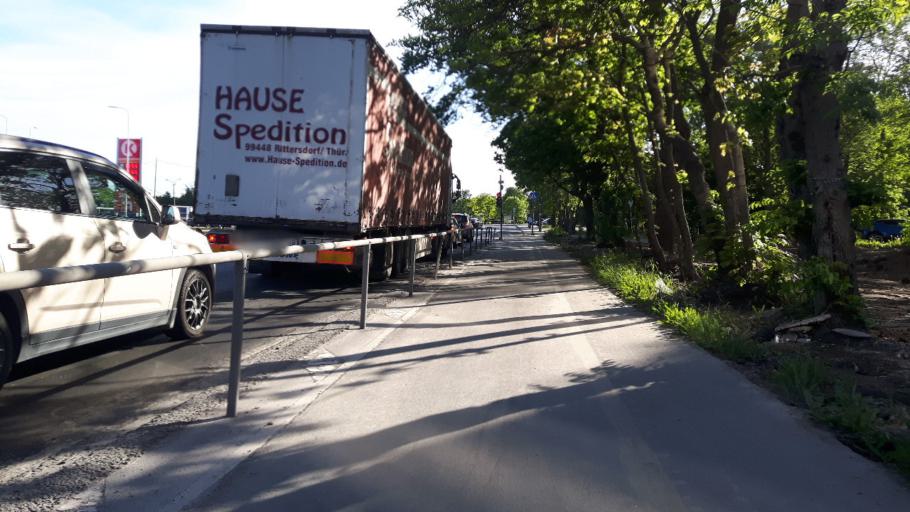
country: EE
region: Harju
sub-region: Viimsi vald
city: Viimsi
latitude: 59.4453
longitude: 24.8157
